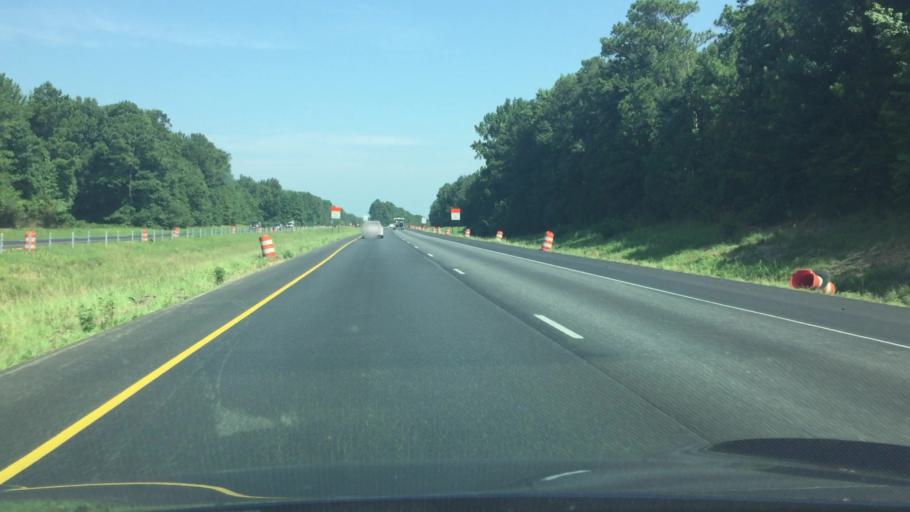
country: US
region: Alabama
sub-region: Chilton County
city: Clanton
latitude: 32.7636
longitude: -86.5613
